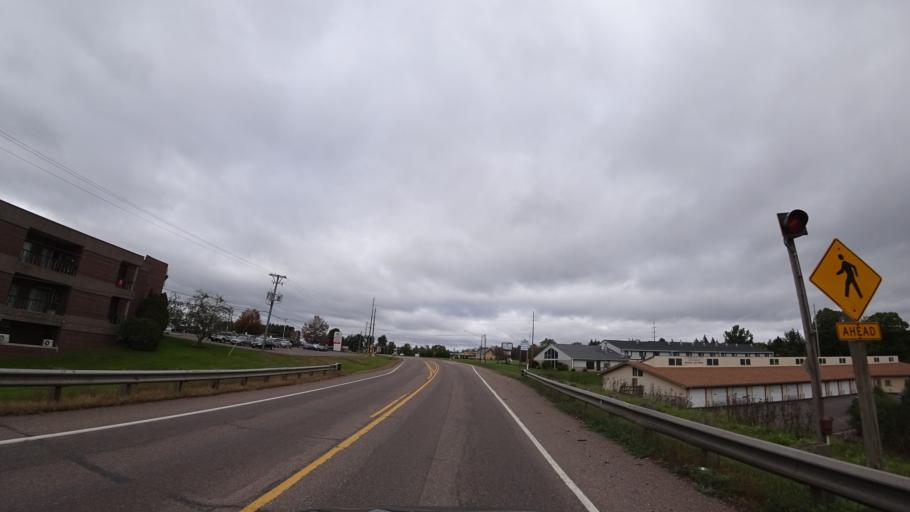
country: US
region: Wisconsin
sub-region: Rusk County
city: Ladysmith
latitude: 45.4543
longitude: -91.1089
